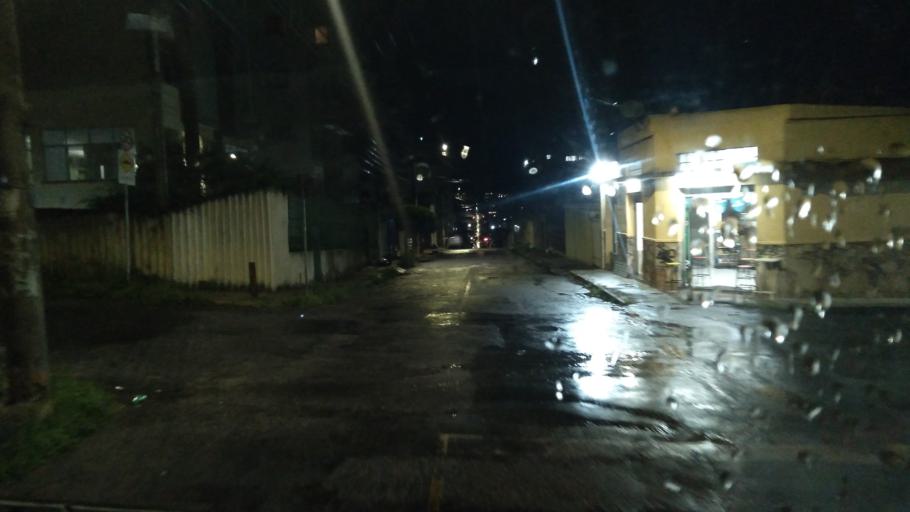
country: BR
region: Minas Gerais
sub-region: Belo Horizonte
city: Belo Horizonte
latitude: -19.9093
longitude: -43.9795
